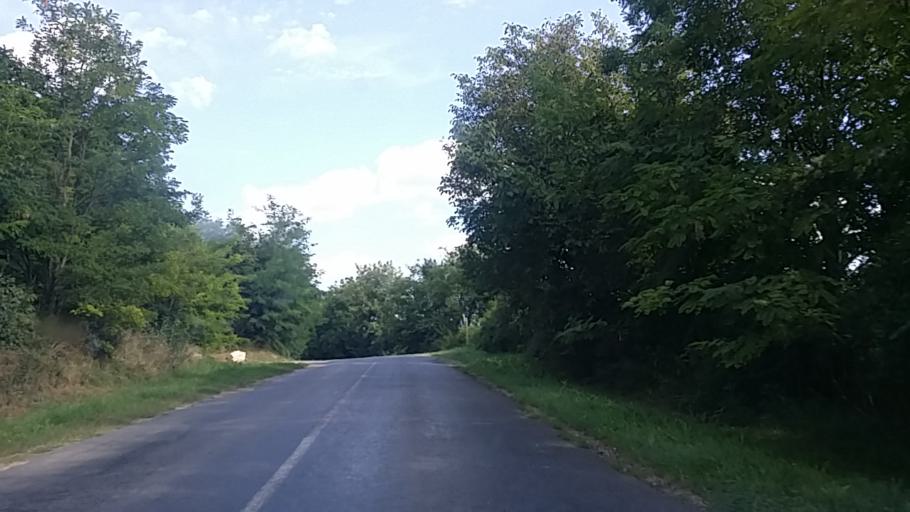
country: HU
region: Tolna
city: Gyonk
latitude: 46.5133
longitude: 18.5357
